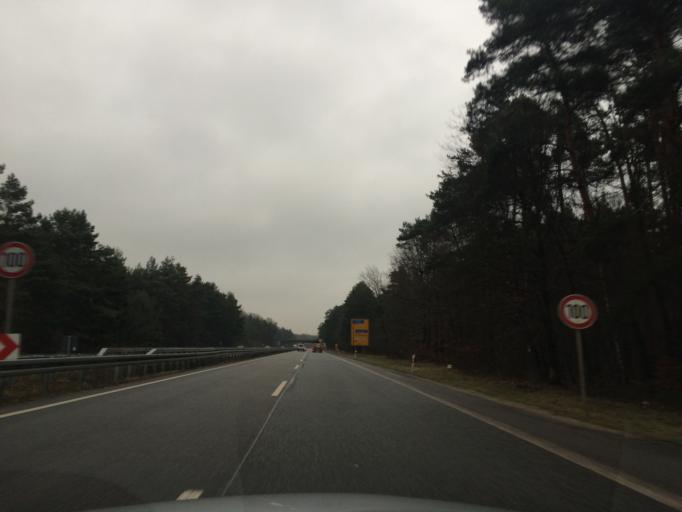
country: DE
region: Hesse
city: Morfelden-Walldorf
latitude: 50.0265
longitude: 8.6135
